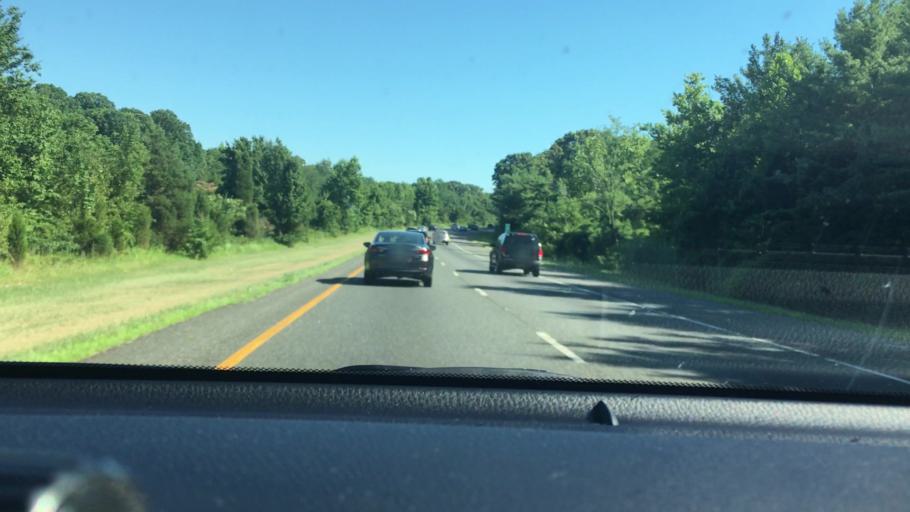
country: US
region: New Jersey
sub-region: Camden County
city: Blackwood
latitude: 39.8087
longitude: -75.1054
